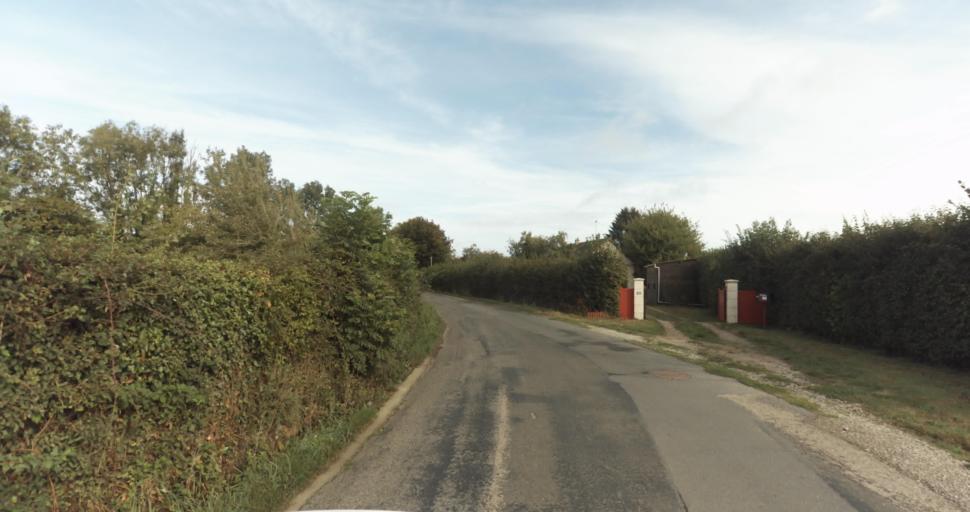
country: FR
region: Lower Normandy
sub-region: Departement de l'Orne
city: Gace
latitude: 48.8974
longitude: 0.3321
